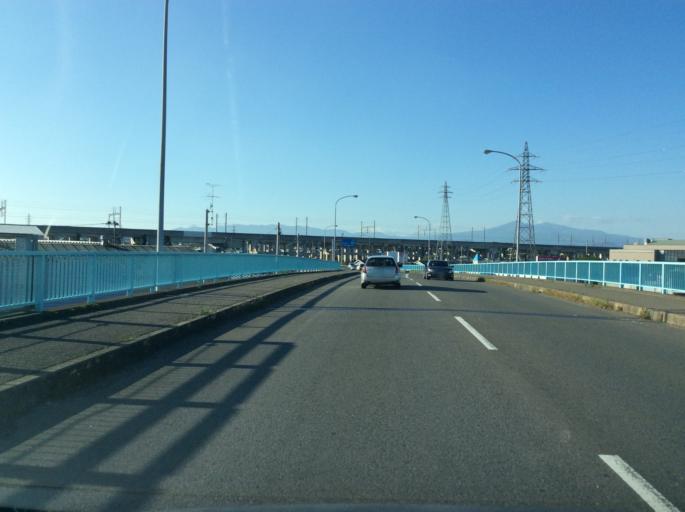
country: JP
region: Fukushima
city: Koriyama
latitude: 37.4112
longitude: 140.3958
